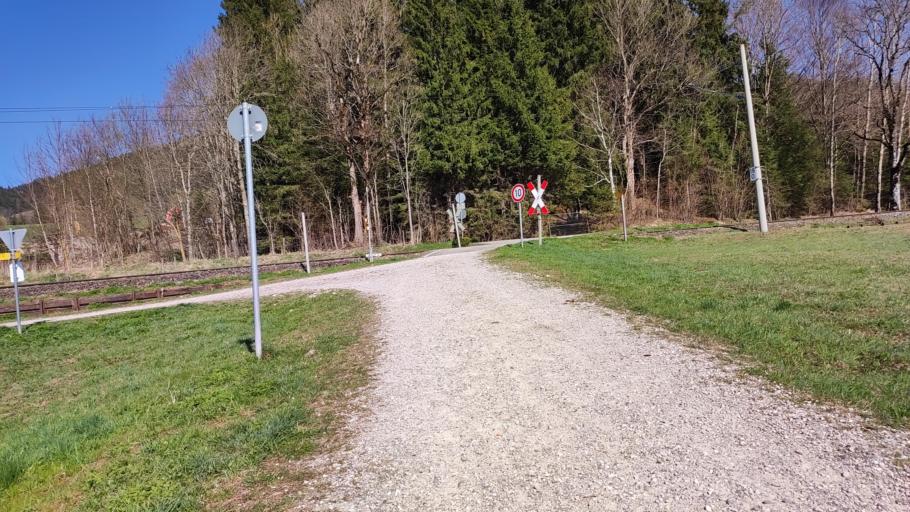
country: DE
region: Bavaria
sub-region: Upper Bavaria
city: Unterammergau
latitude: 47.6382
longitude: 11.0260
